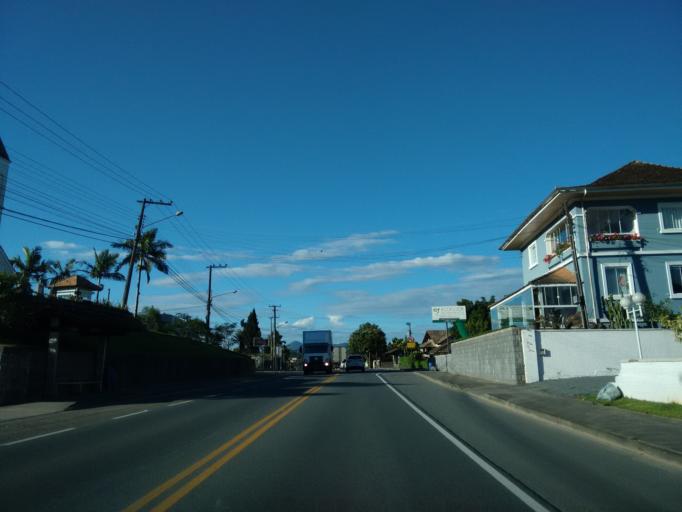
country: BR
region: Santa Catarina
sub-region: Pomerode
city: Pomerode
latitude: -26.7534
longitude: -49.1733
